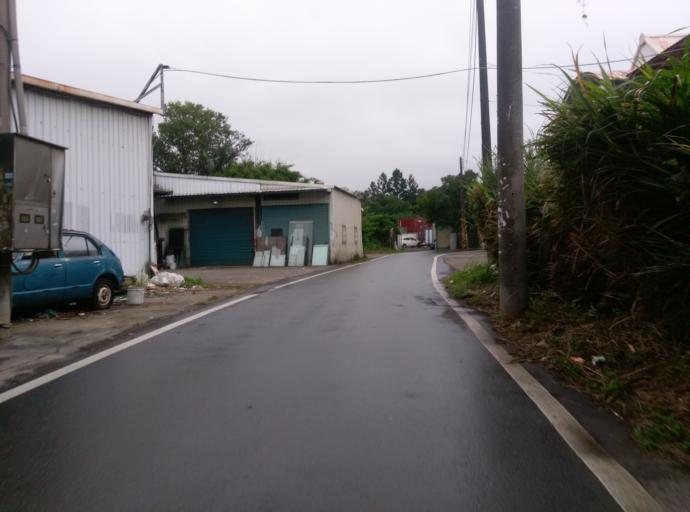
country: TW
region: Taiwan
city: Daxi
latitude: 24.9101
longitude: 121.2432
